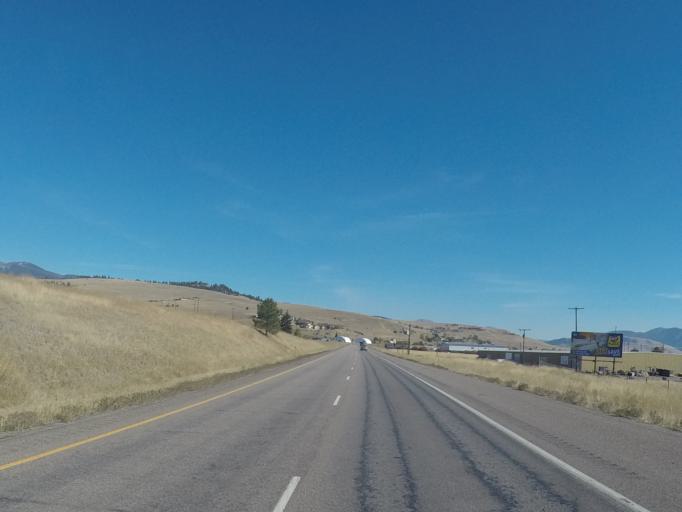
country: US
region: Montana
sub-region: Missoula County
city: Orchard Homes
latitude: 46.9384
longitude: -114.1065
